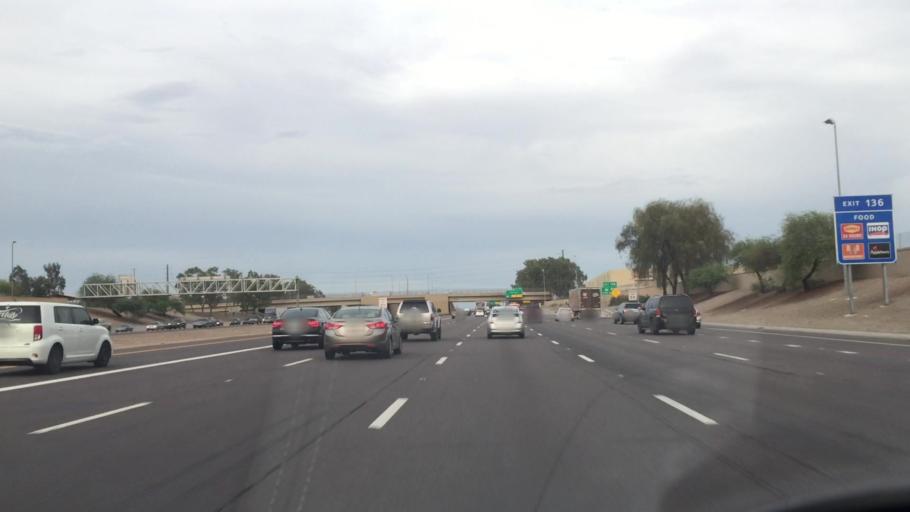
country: US
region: Arizona
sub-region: Maricopa County
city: Tolleson
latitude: 33.4615
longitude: -112.2324
